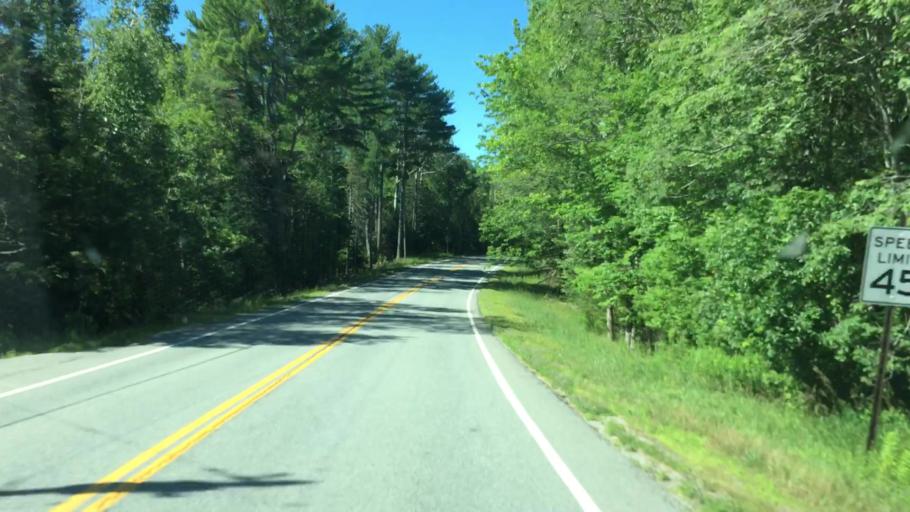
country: US
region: Maine
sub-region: Hancock County
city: Dedham
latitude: 44.6886
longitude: -68.6611
